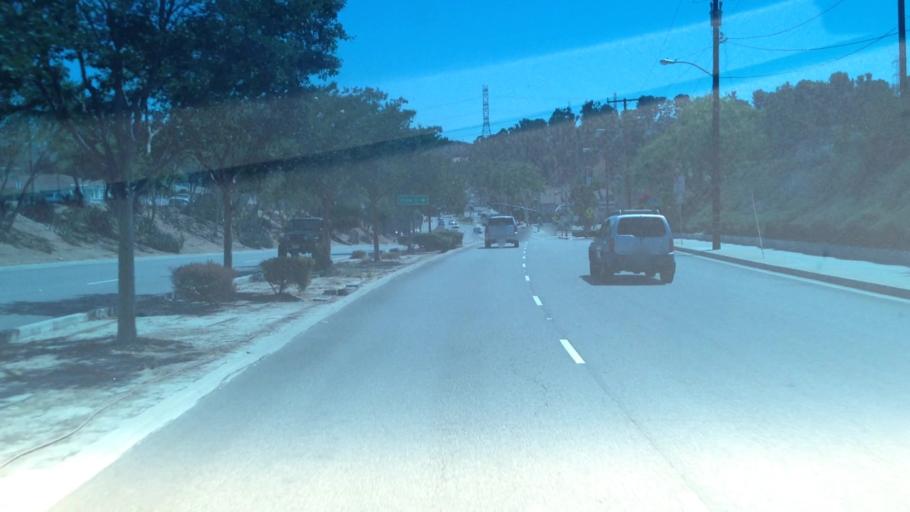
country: US
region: California
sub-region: Los Angeles County
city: South San Gabriel
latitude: 34.0435
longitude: -118.0909
